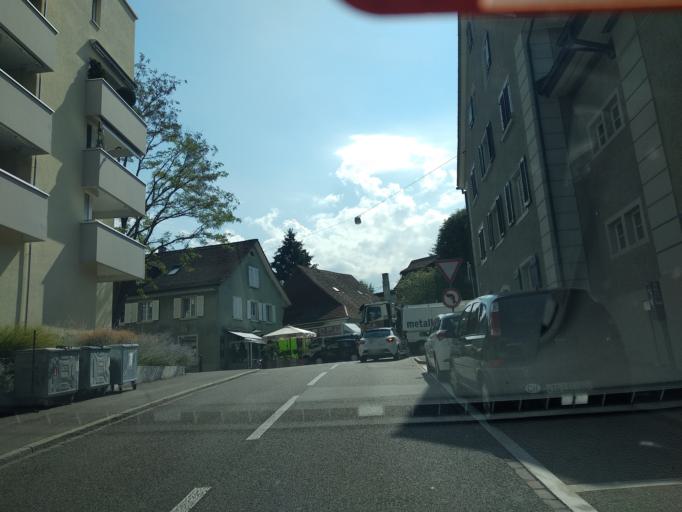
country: CH
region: Thurgau
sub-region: Frauenfeld District
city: Frauenfeld
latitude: 47.5596
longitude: 8.9008
